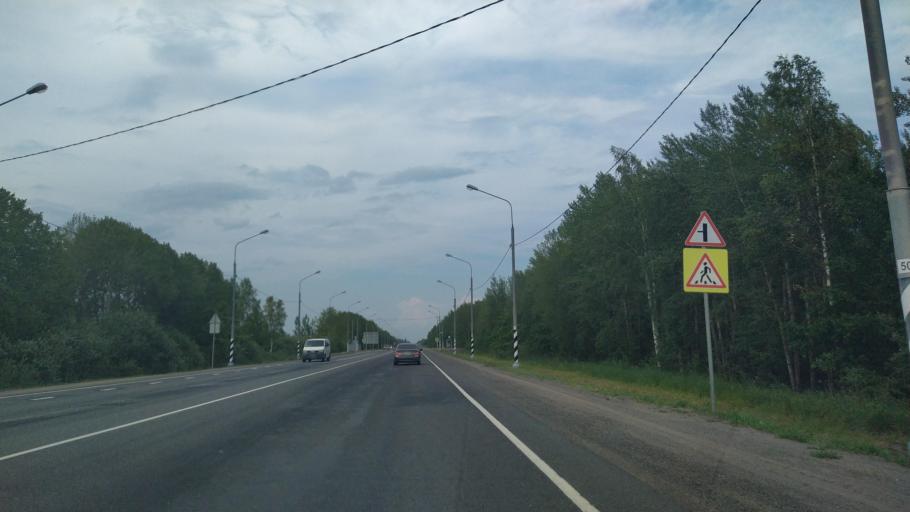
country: RU
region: Novgorod
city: Pankovka
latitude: 58.4427
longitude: 31.1198
